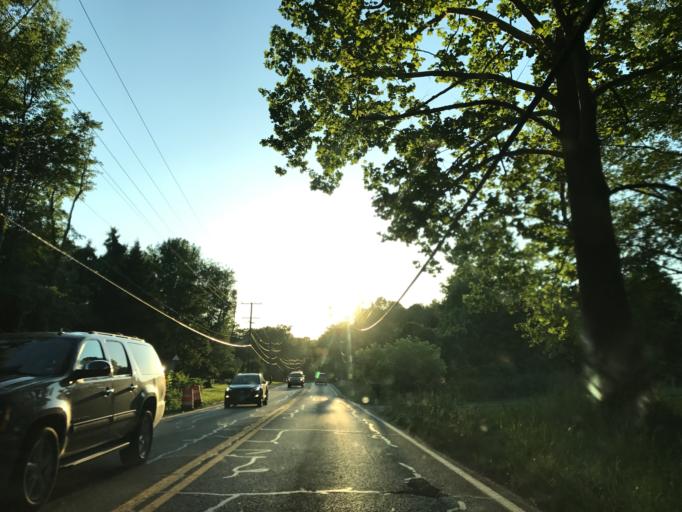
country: US
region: Maryland
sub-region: Anne Arundel County
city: Londontowne
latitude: 38.9133
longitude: -76.5449
